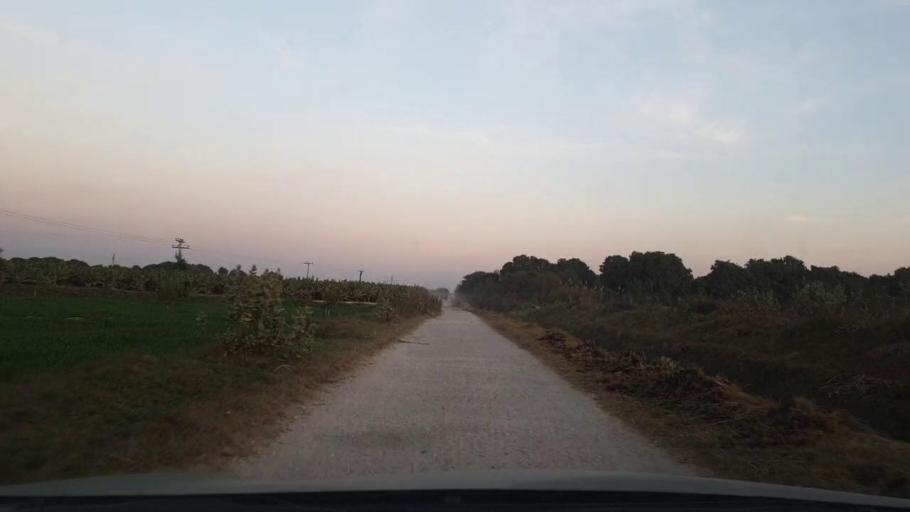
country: PK
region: Sindh
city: Tando Allahyar
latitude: 25.5618
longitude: 68.7694
